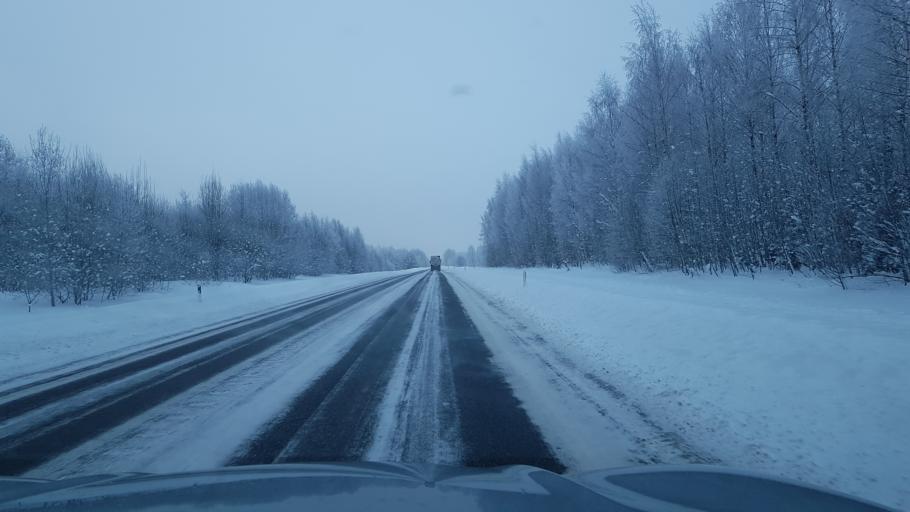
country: EE
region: Ida-Virumaa
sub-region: Johvi vald
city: Johvi
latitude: 59.2156
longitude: 27.3394
